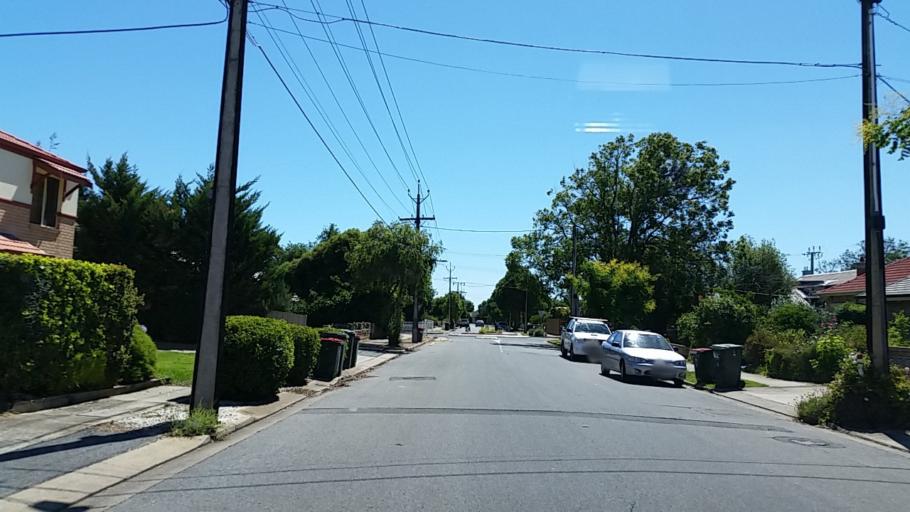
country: AU
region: South Australia
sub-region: Marion
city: South Plympton
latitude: -34.9742
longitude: 138.5676
